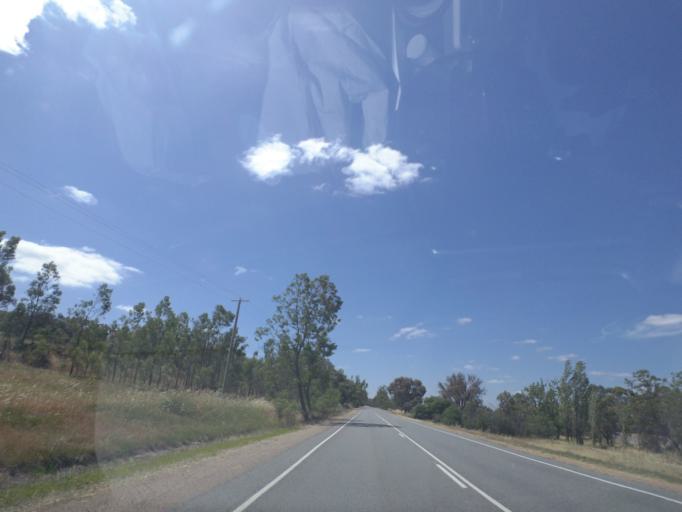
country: AU
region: Victoria
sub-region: Wangaratta
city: Wangaratta
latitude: -36.4563
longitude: 146.2367
